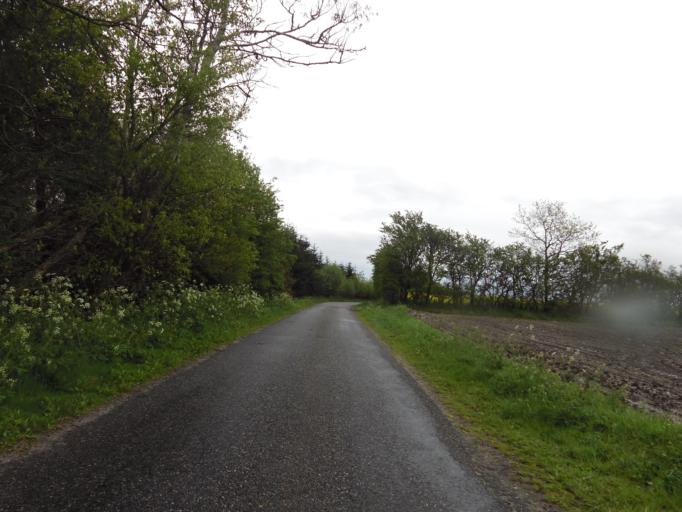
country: DK
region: South Denmark
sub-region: Tonder Kommune
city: Sherrebek
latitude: 55.2117
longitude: 8.9030
